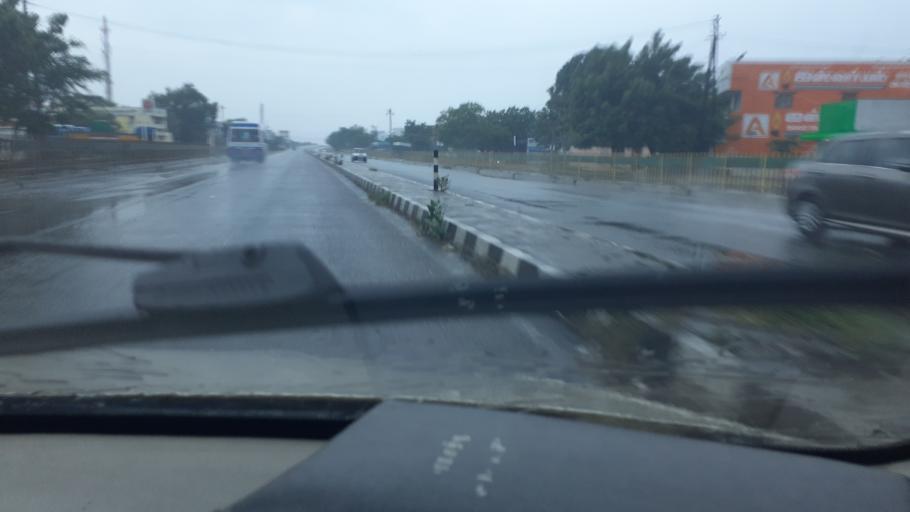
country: IN
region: Tamil Nadu
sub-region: Virudhunagar
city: Sattur
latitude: 9.3720
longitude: 77.9128
